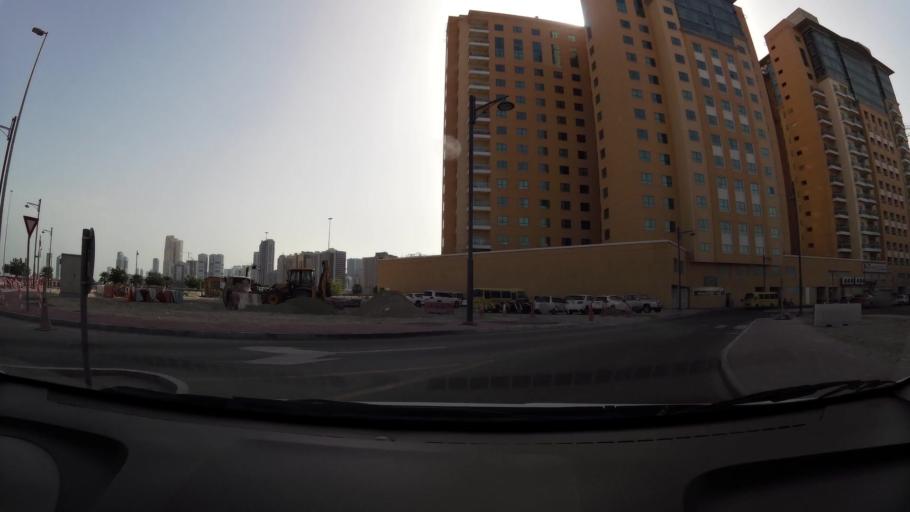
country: AE
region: Ash Shariqah
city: Sharjah
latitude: 25.2890
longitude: 55.3564
